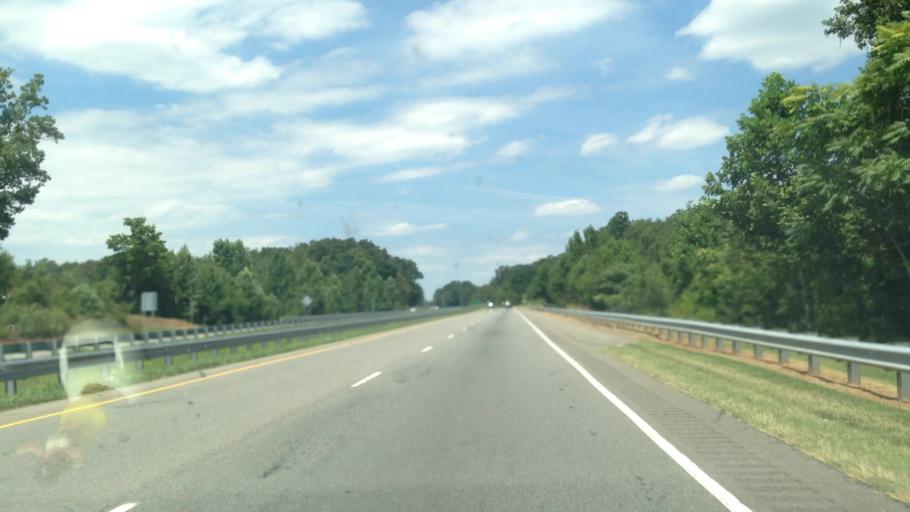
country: US
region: North Carolina
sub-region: Rockingham County
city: Stoneville
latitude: 36.4932
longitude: -79.9240
